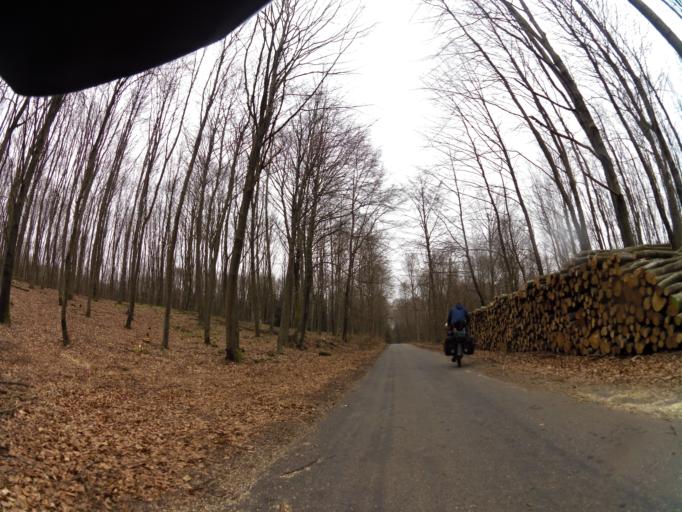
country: PL
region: West Pomeranian Voivodeship
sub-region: Powiat koszalinski
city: Bobolice
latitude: 53.9456
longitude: 16.6704
